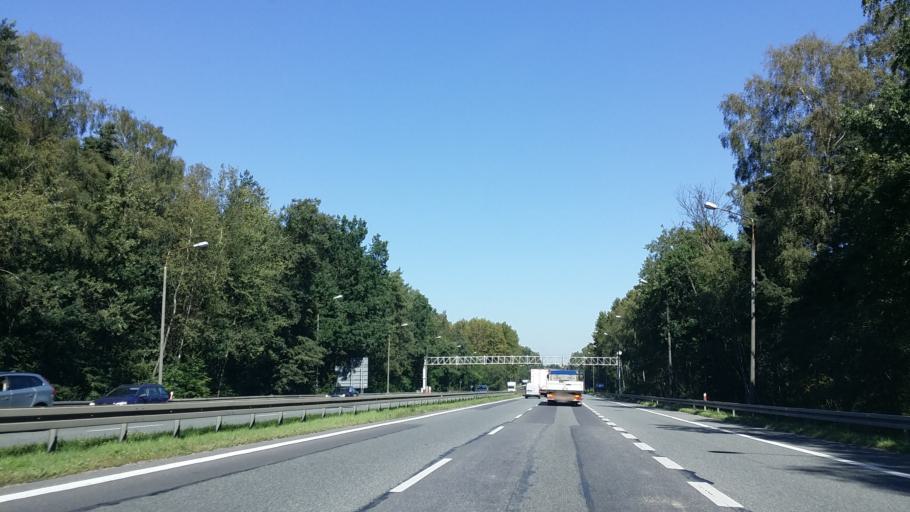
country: PL
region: Silesian Voivodeship
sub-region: Myslowice
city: Myslowice
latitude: 50.1777
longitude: 19.1686
